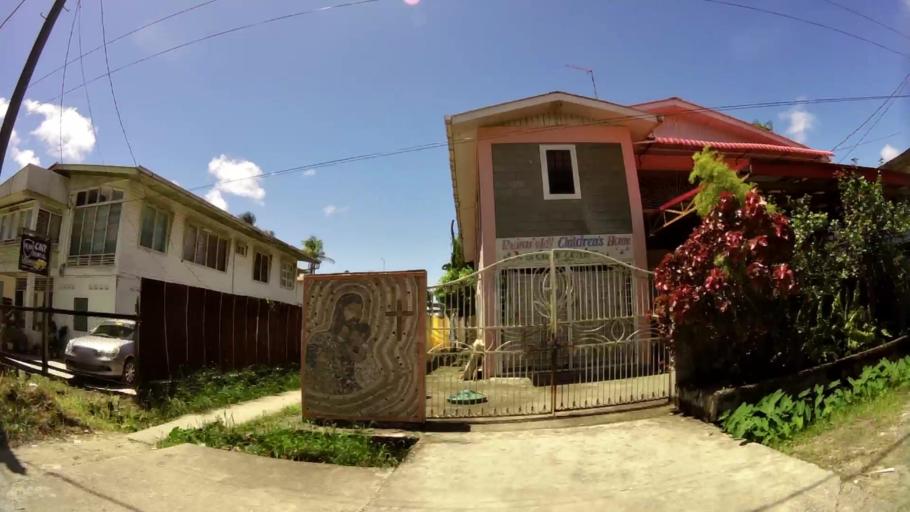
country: GY
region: Demerara-Mahaica
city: Georgetown
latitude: 6.7927
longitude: -58.1475
